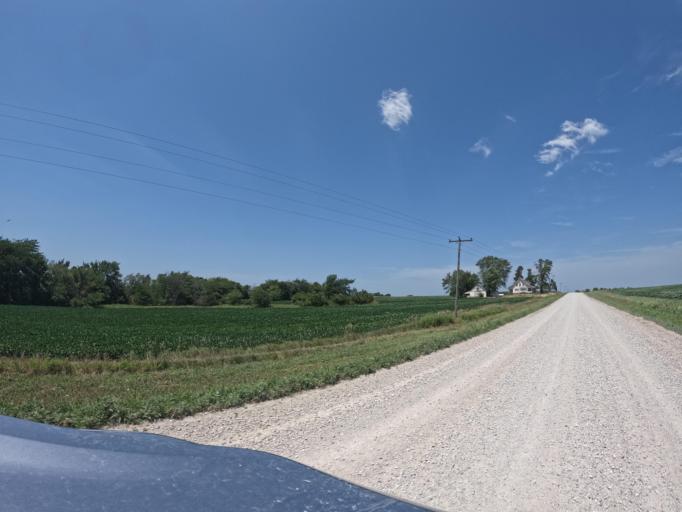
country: US
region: Iowa
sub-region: Henry County
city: Mount Pleasant
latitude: 40.9356
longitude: -91.6457
